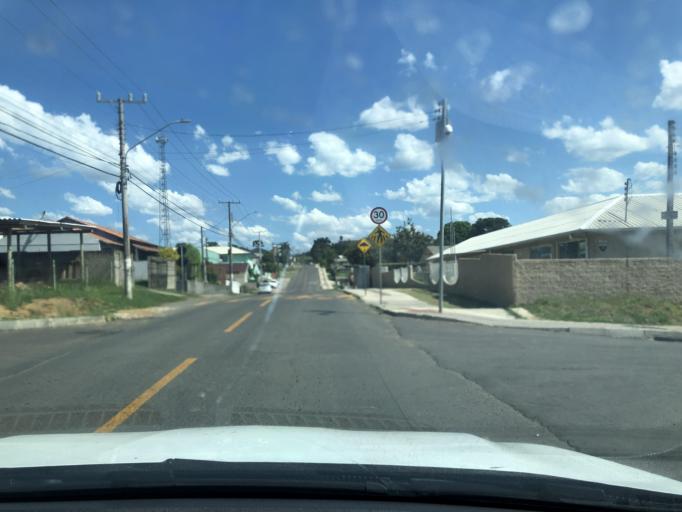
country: BR
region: Santa Catarina
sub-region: Lages
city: Lages
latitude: -27.7967
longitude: -50.3382
